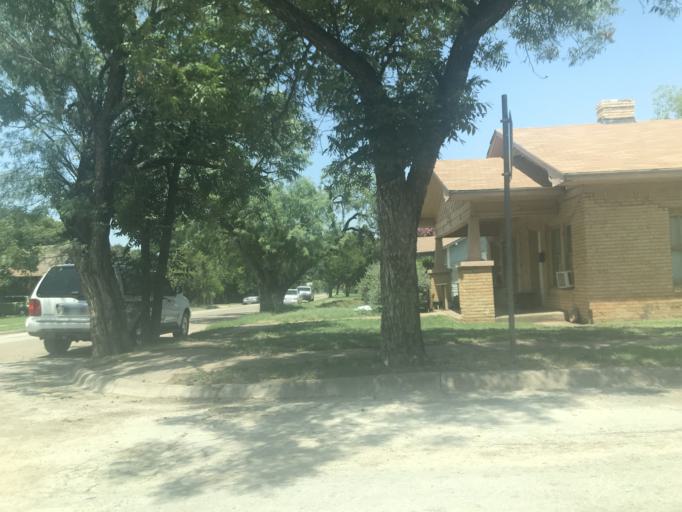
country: US
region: Texas
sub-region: Taylor County
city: Abilene
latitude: 32.4482
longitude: -99.7509
